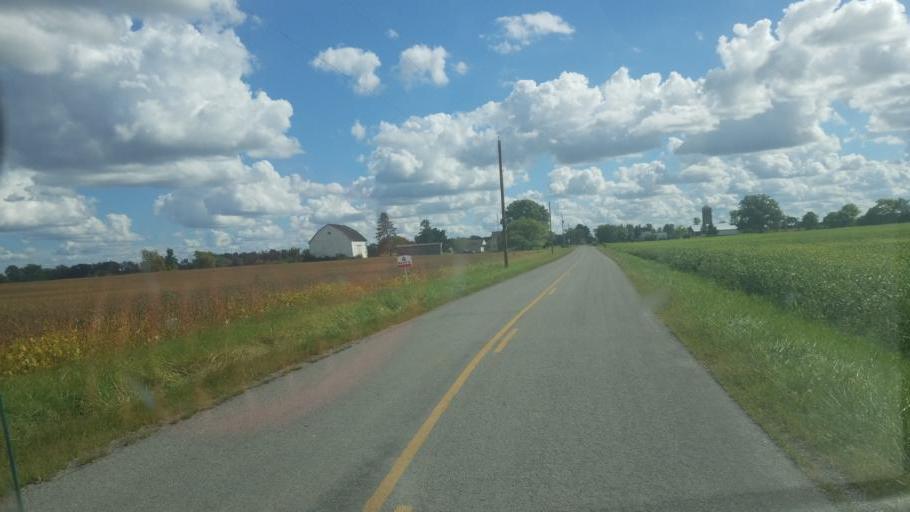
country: US
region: Ohio
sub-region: Hardin County
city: Kenton
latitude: 40.5081
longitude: -83.5511
